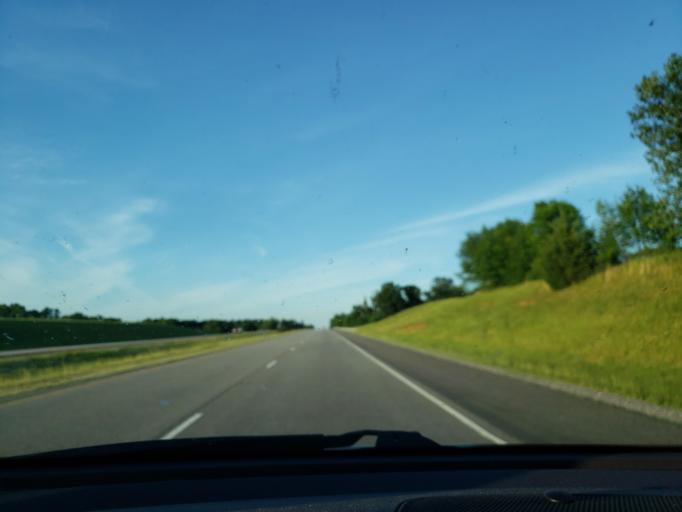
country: US
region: Virginia
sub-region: Henrico County
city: Fort Lee
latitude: 37.4643
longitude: -77.3743
